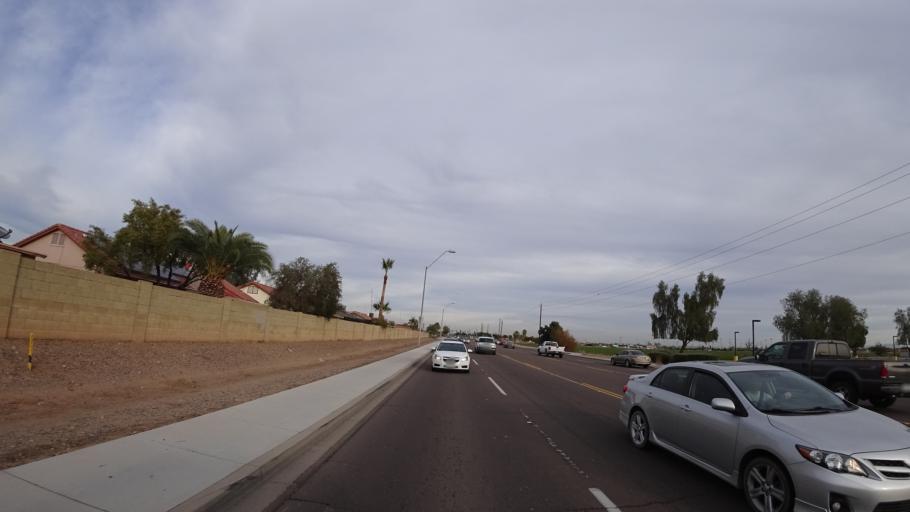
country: US
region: Arizona
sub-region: Maricopa County
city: Peoria
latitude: 33.5665
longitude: -112.2415
